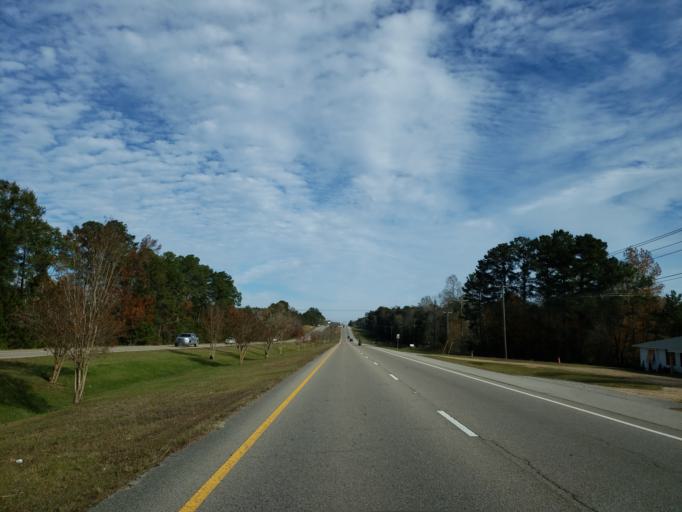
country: US
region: Mississippi
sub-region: Lamar County
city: West Hattiesburg
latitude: 31.3134
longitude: -89.4653
